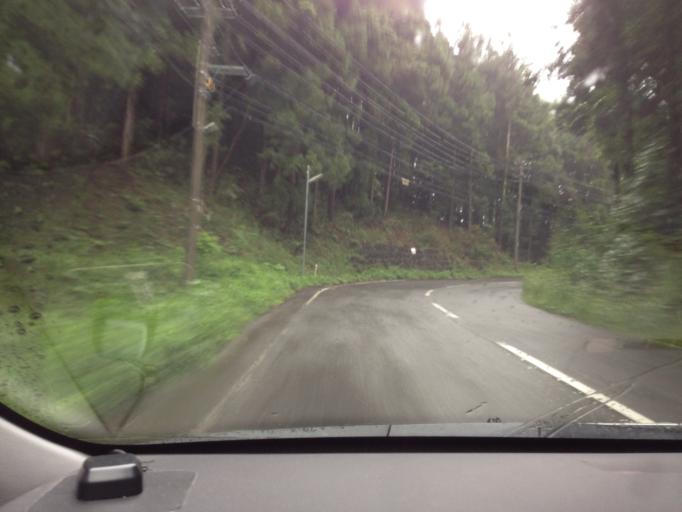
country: JP
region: Fukushima
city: Koriyama
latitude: 37.4391
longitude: 140.2621
